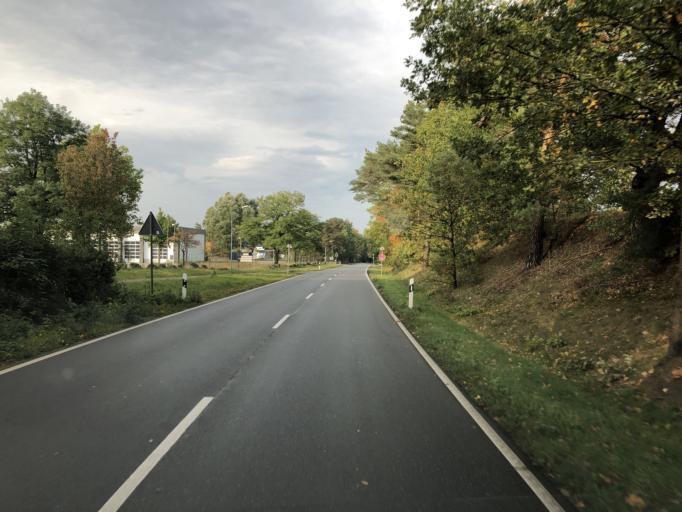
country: DE
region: Lower Saxony
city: Neu Wulmstorf
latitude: 53.4522
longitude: 9.7994
